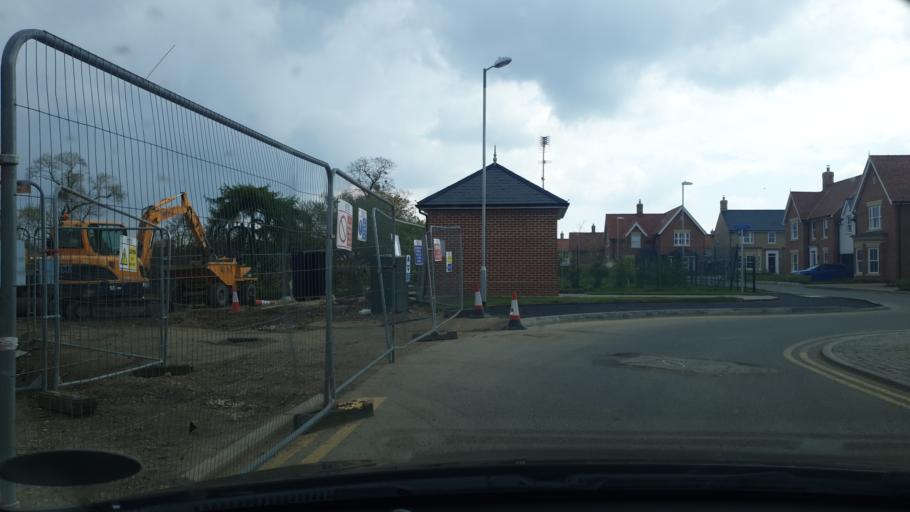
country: GB
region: England
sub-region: Essex
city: Manningtree
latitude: 51.9423
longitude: 1.0488
